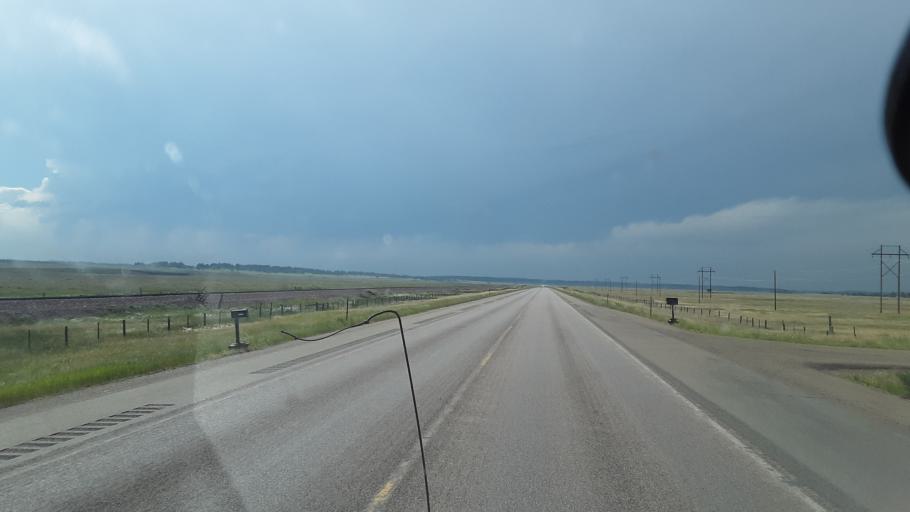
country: US
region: South Dakota
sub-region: Butte County
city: Belle Fourche
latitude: 44.8175
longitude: -104.0657
